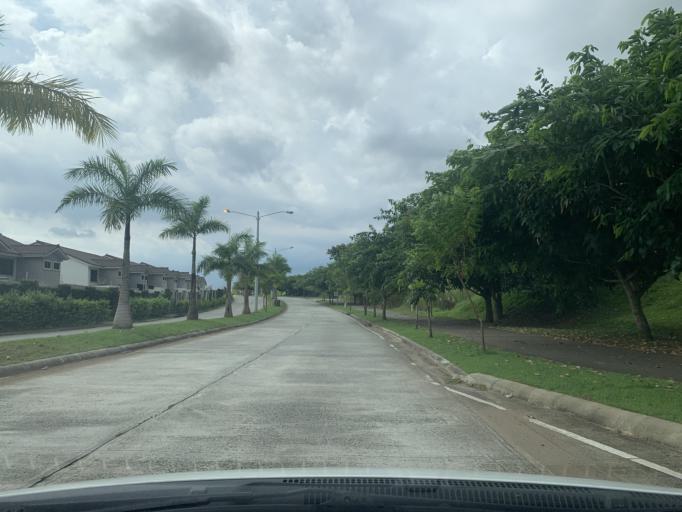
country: PA
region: Panama
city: San Miguelito
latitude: 9.0881
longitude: -79.4634
